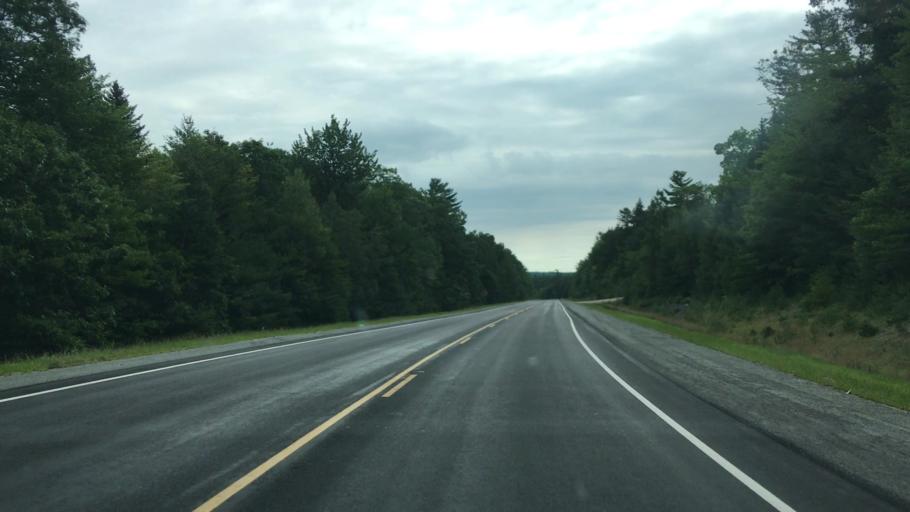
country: US
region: Maine
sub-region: Washington County
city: Addison
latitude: 44.9106
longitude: -67.8510
